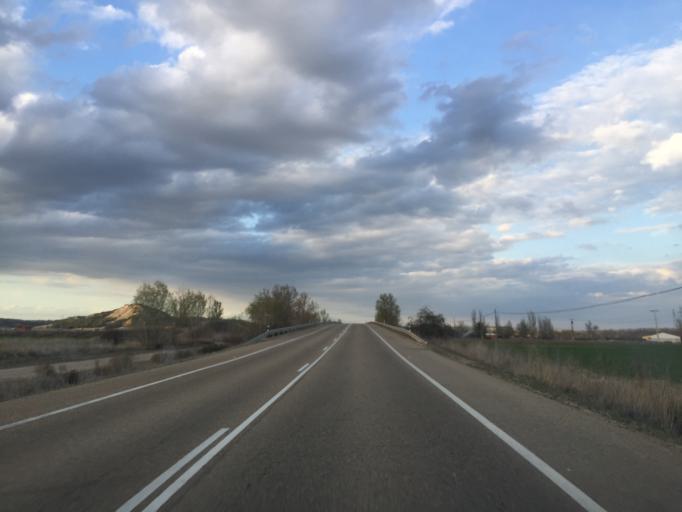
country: ES
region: Castille and Leon
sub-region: Provincia de Palencia
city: Soto de Cerrato
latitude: 41.9633
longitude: -4.4477
